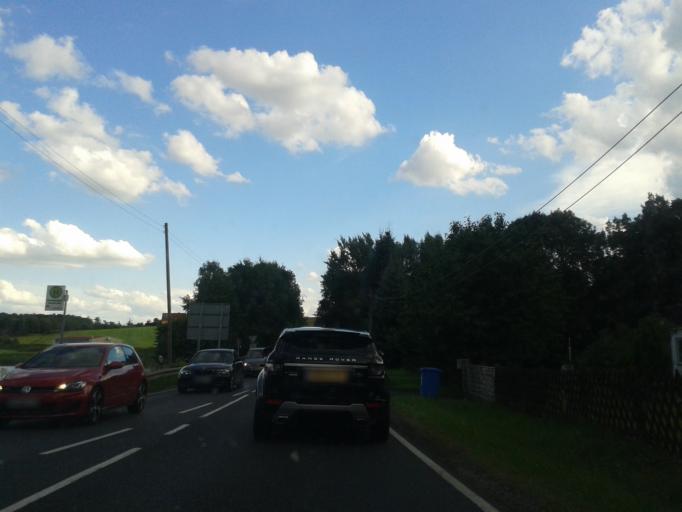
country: DE
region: Saxony
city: Radeberg
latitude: 51.0630
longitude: 13.9343
